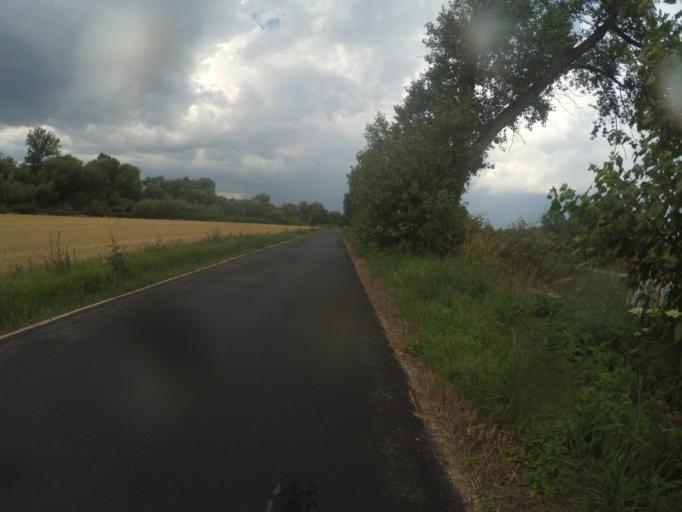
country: CZ
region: Central Bohemia
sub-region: Okres Melnik
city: Melnik
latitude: 50.3642
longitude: 14.4552
